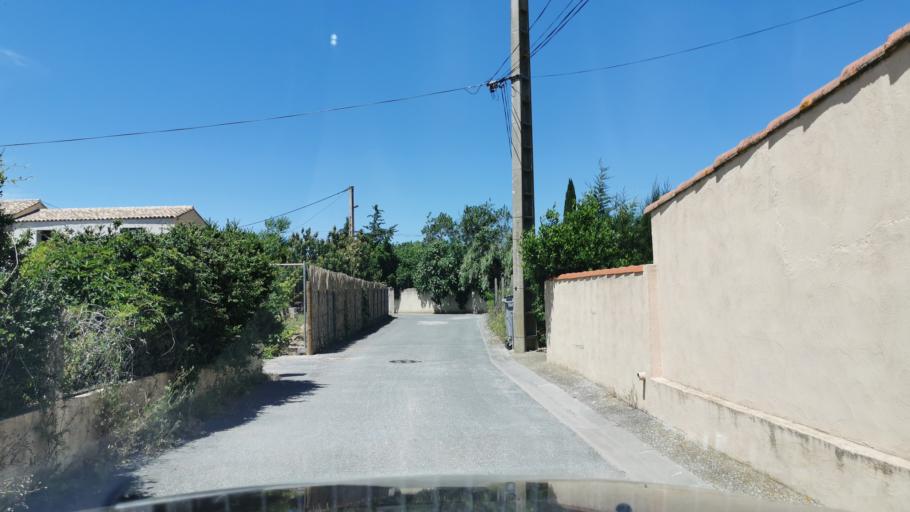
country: FR
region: Languedoc-Roussillon
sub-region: Departement de l'Aude
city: Canet
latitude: 43.2148
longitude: 2.8581
